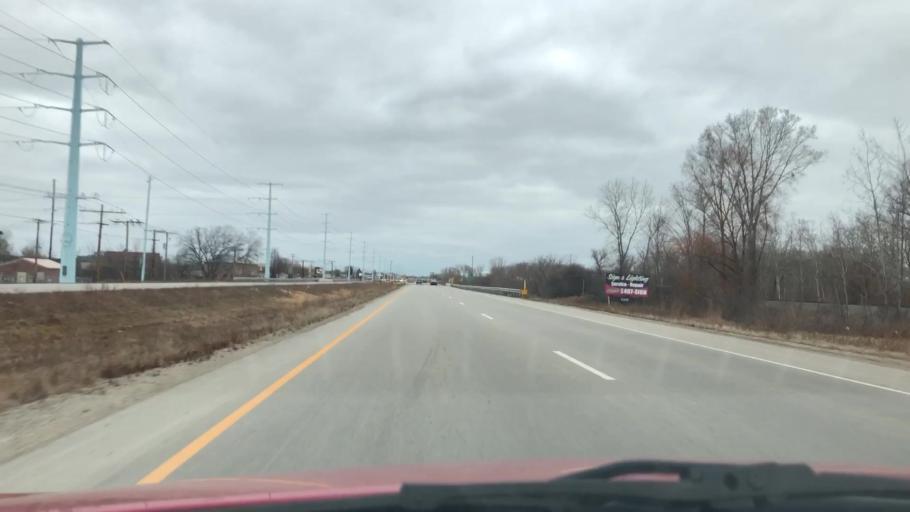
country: US
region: Wisconsin
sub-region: Brown County
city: De Pere
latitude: 44.4639
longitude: -88.0707
